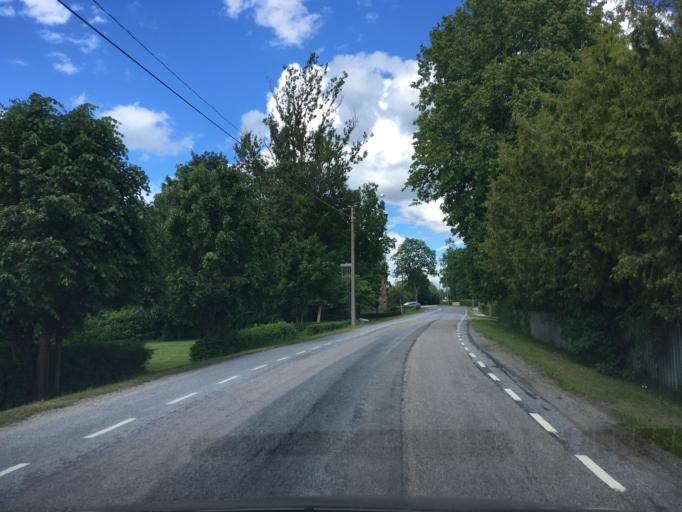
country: EE
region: Paernumaa
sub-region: Halinga vald
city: Parnu-Jaagupi
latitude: 58.6187
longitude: 24.5330
